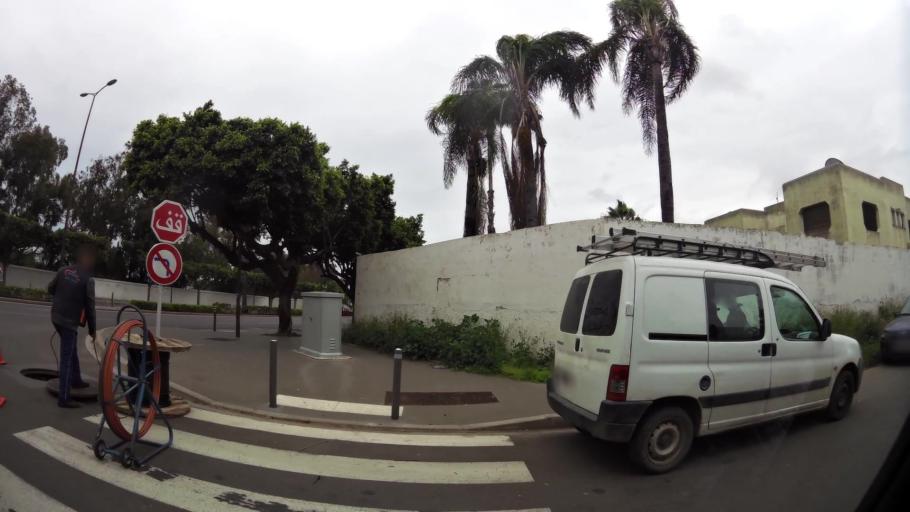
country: MA
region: Grand Casablanca
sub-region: Casablanca
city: Casablanca
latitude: 33.5837
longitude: -7.6570
